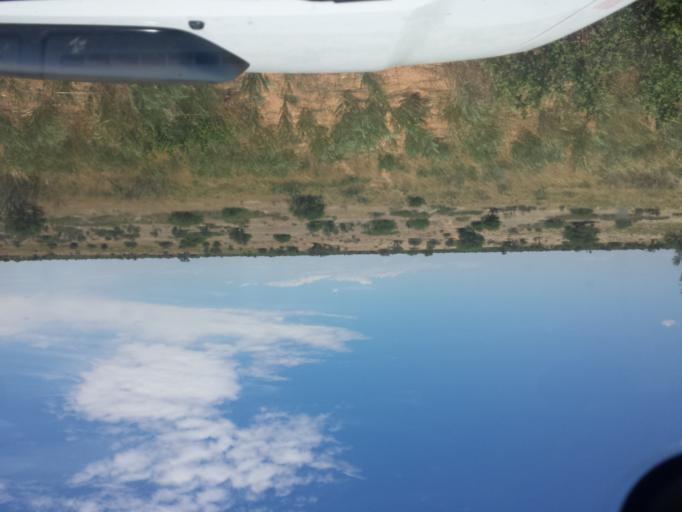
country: BW
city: Lokwabe
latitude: -24.9222
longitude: 21.6238
